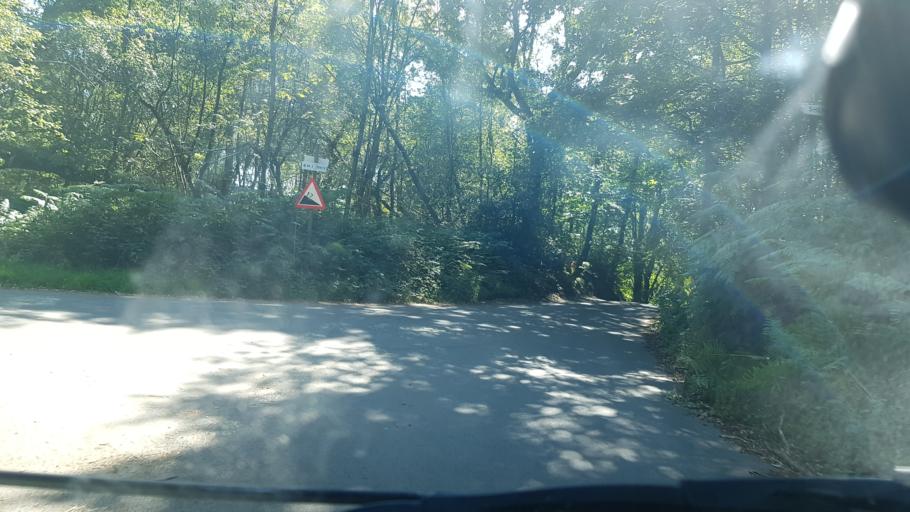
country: GB
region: England
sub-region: Surrey
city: Cranleigh
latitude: 51.1747
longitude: -0.4872
